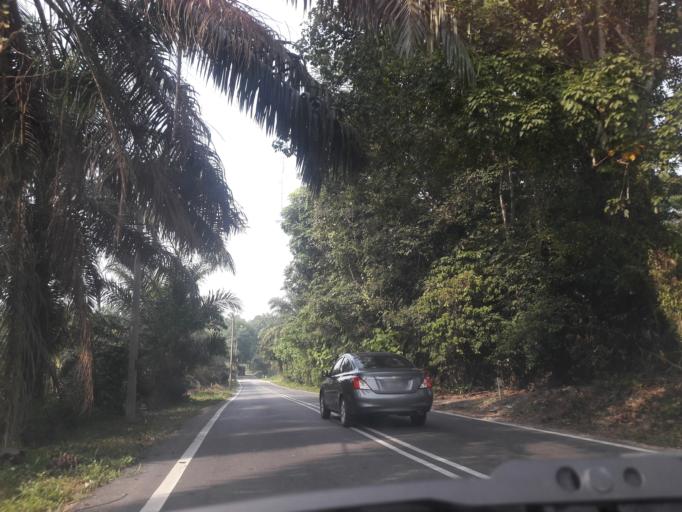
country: MY
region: Kedah
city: Kulim
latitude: 5.3575
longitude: 100.5209
